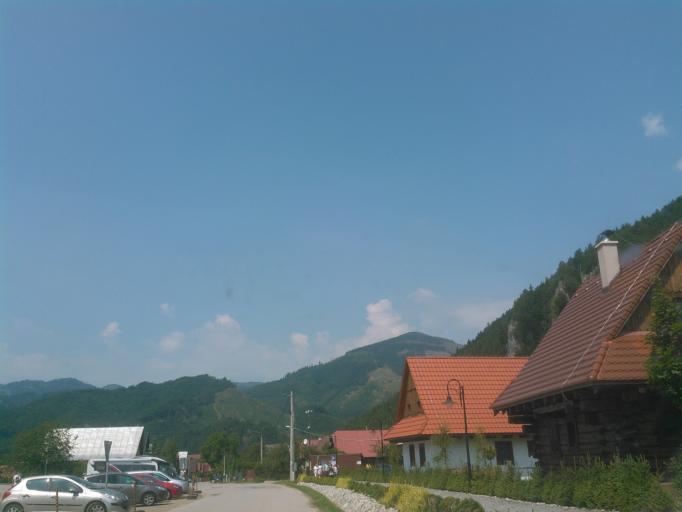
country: SK
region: Zilinsky
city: Ruzomberok
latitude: 48.9488
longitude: 19.2757
